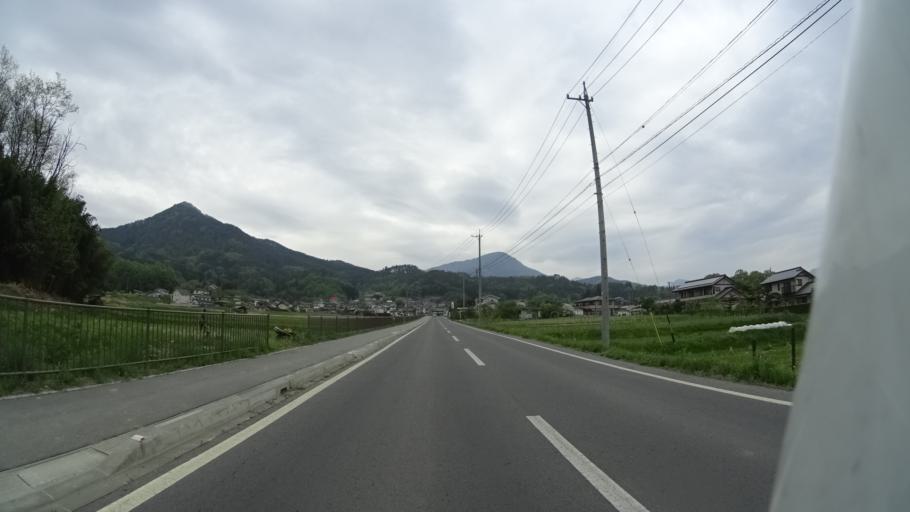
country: JP
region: Nagano
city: Kamimaruko
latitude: 36.3508
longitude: 138.1750
